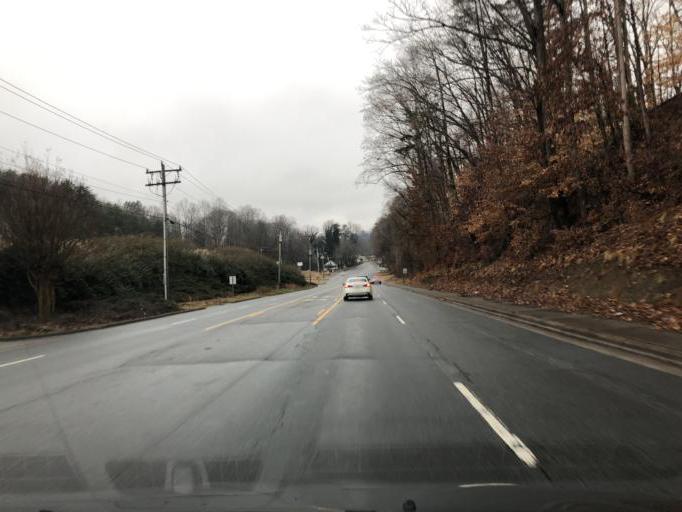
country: US
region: North Carolina
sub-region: Rutherford County
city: Rutherfordton
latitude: 35.3646
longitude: -81.9479
